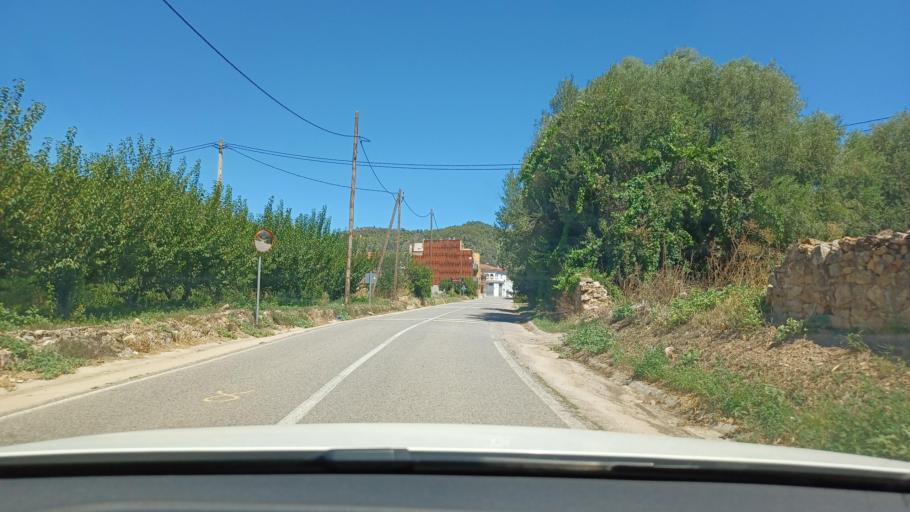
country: ES
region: Catalonia
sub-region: Provincia de Tarragona
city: Benifallet
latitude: 40.9715
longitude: 0.5155
